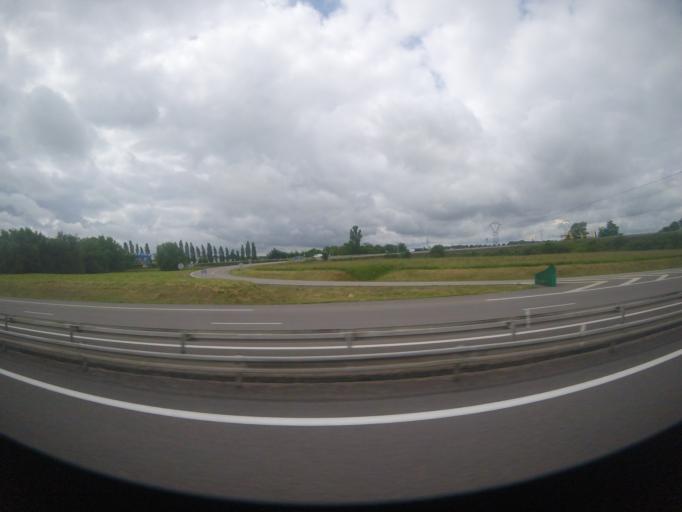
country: FR
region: Lorraine
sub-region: Departement de la Moselle
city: Sainte-Marie-aux-Chenes
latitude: 49.1941
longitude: 5.9902
